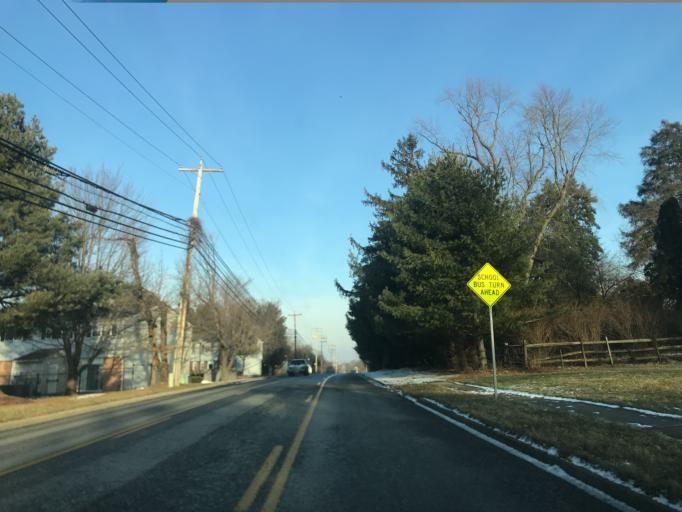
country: US
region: Maryland
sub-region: Harford County
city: Edgewood
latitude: 39.4236
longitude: -76.3185
